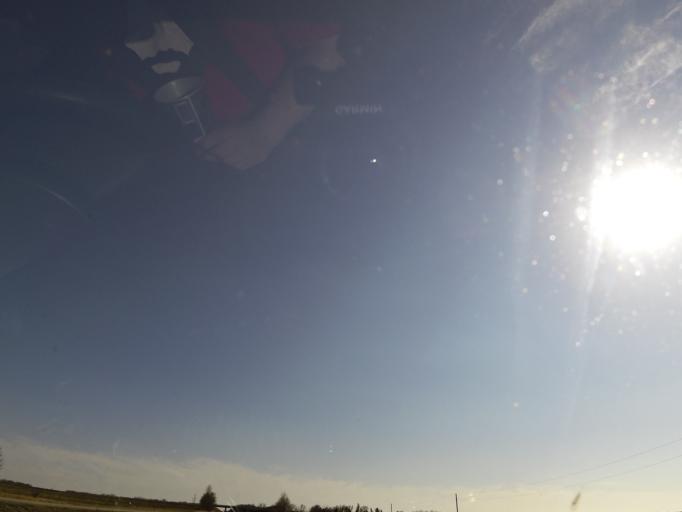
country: US
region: Minnesota
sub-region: Steele County
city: Owatonna
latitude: 44.0125
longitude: -93.2540
